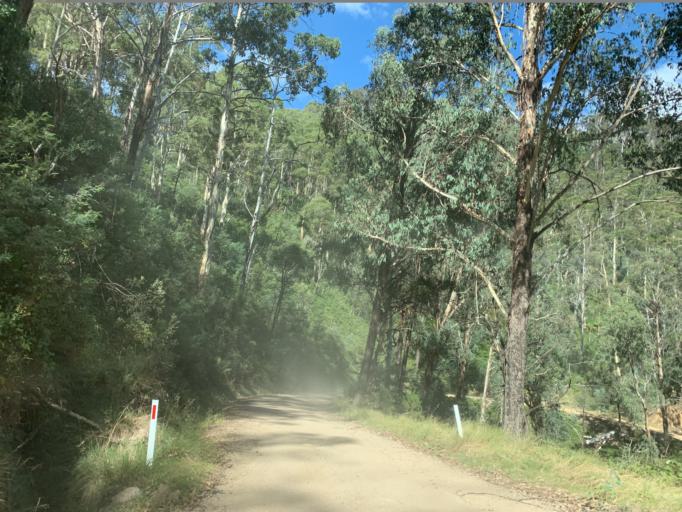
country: AU
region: Victoria
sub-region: Mansfield
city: Mansfield
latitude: -37.0932
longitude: 146.5267
